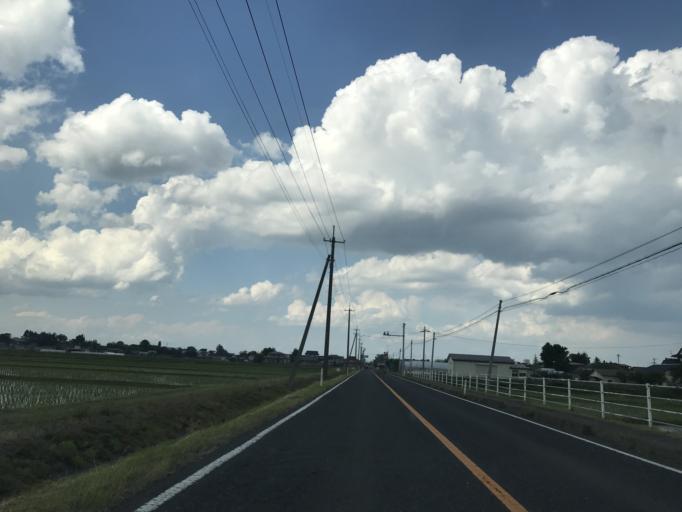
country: JP
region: Miyagi
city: Wakuya
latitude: 38.6072
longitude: 141.1738
